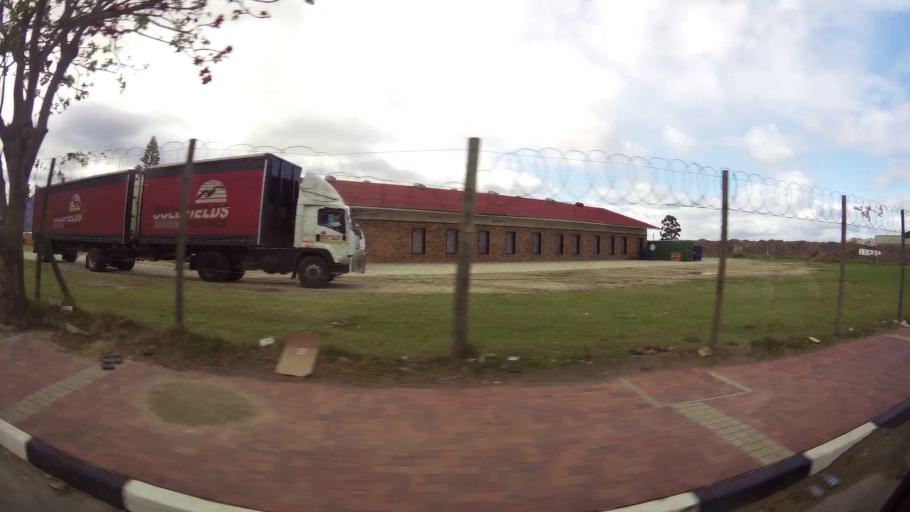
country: ZA
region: Western Cape
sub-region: Eden District Municipality
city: George
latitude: -33.9737
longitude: 22.4714
